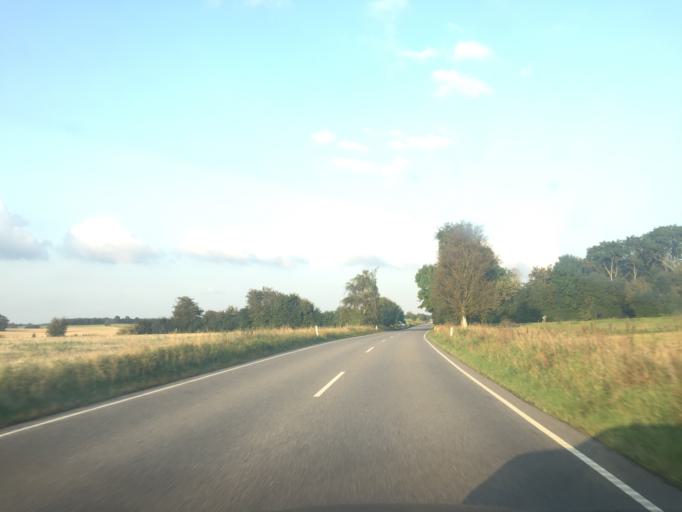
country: DK
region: Zealand
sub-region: Holbaek Kommune
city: Tollose
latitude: 55.5571
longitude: 11.7644
